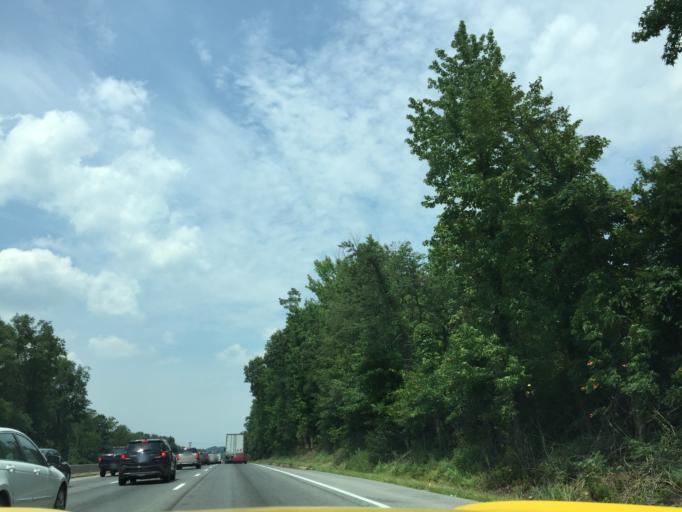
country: US
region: Maryland
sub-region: Prince George's County
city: Friendly
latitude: 38.7531
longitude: -76.9928
